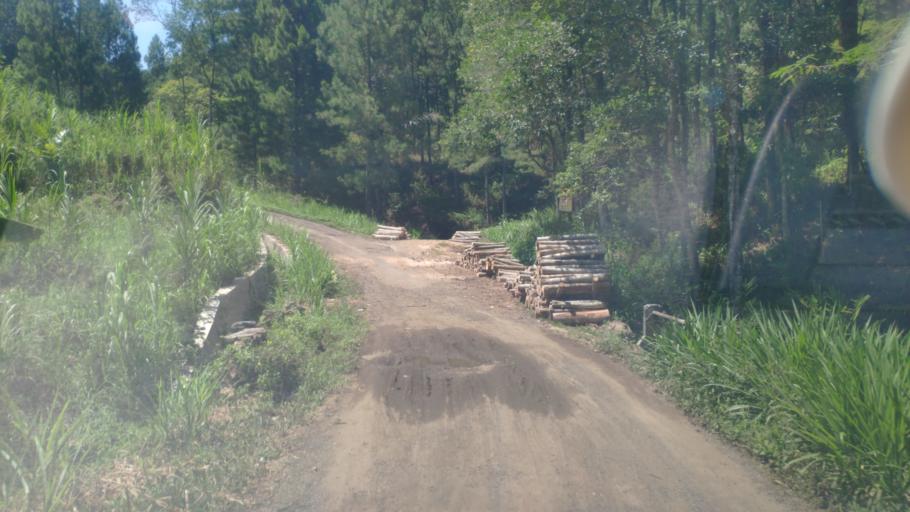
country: ID
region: Central Java
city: Buaran
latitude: -7.2853
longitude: 109.6036
